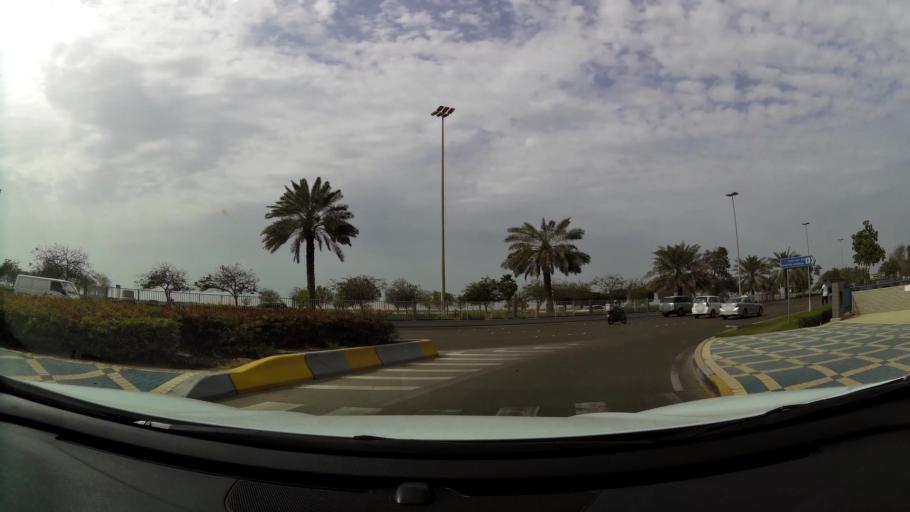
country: AE
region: Abu Dhabi
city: Abu Dhabi
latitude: 24.4821
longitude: 54.3478
